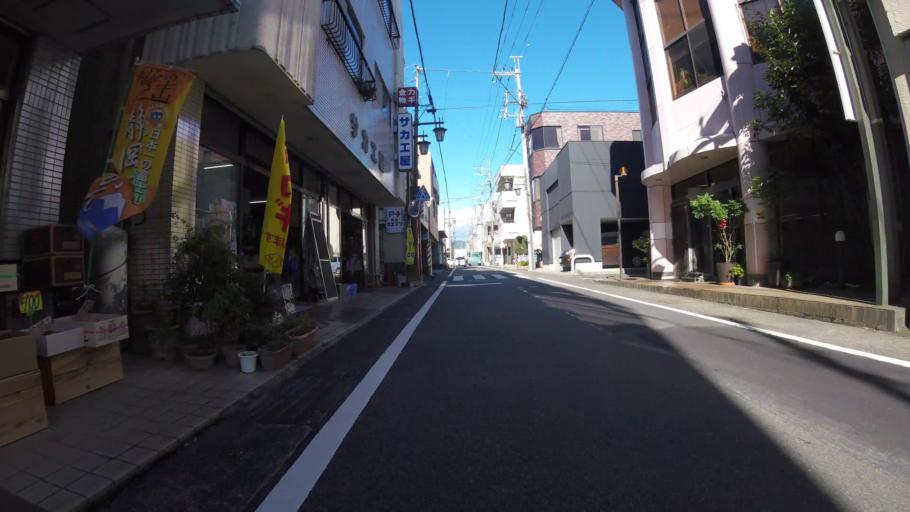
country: JP
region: Shizuoka
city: Mishima
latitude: 35.1300
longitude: 138.8958
